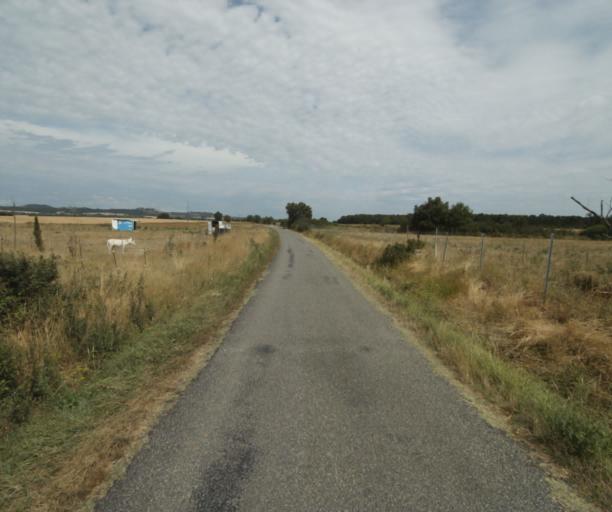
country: FR
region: Midi-Pyrenees
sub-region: Departement de la Haute-Garonne
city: Saint-Felix-Lauragais
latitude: 43.3978
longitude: 1.9090
